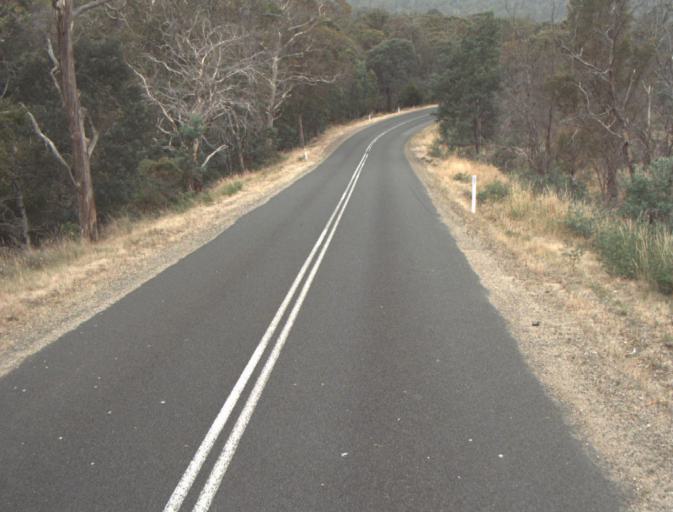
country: AU
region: Tasmania
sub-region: Northern Midlands
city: Evandale
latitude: -41.4954
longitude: 147.3880
